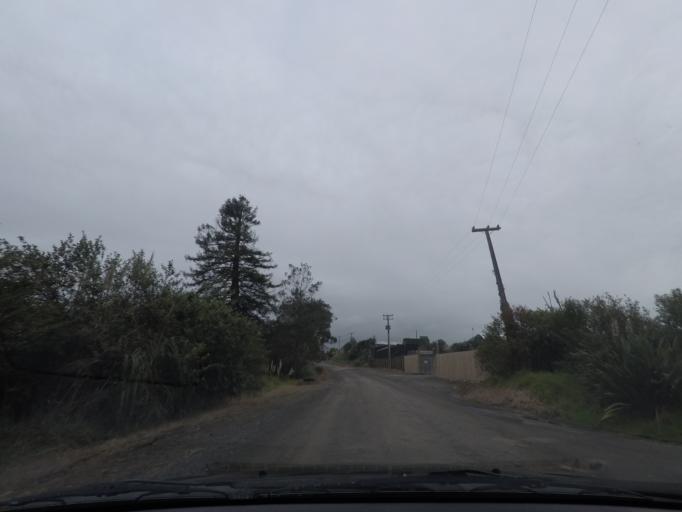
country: NZ
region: Auckland
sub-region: Auckland
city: Muriwai Beach
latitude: -36.7564
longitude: 174.5753
